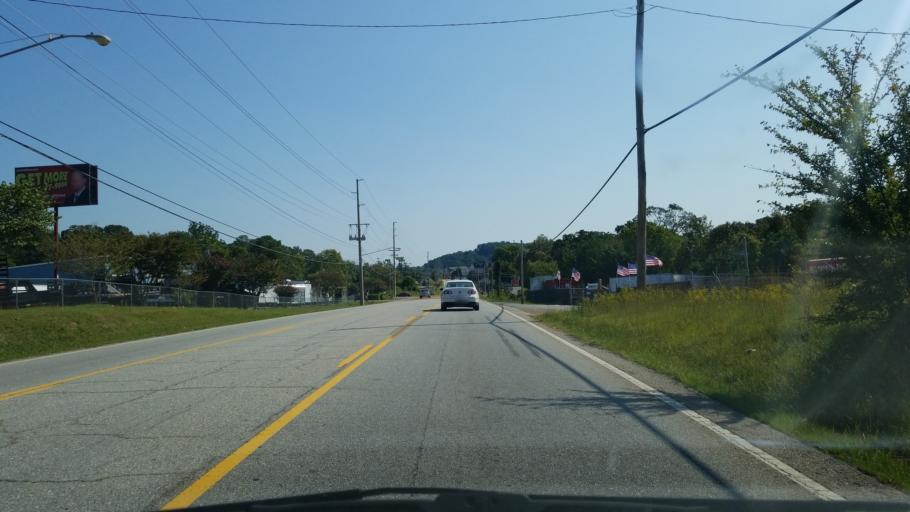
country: US
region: Tennessee
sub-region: Hamilton County
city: Harrison
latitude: 35.0557
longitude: -85.1430
